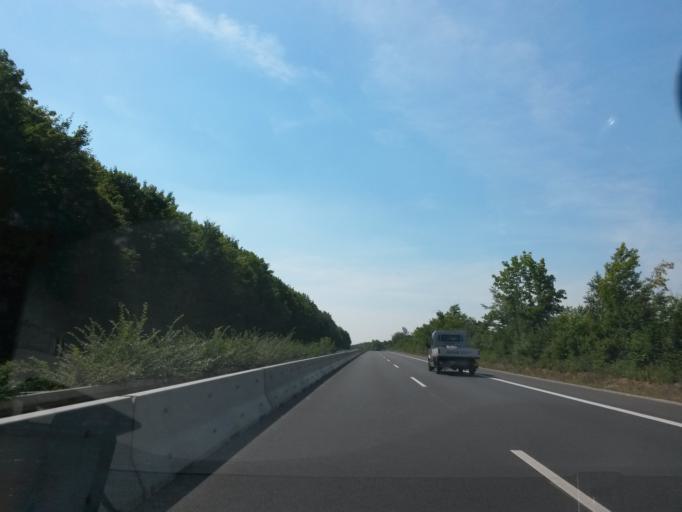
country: DE
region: Bavaria
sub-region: Regierungsbezirk Mittelfranken
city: Seukendorf
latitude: 49.4779
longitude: 10.9190
